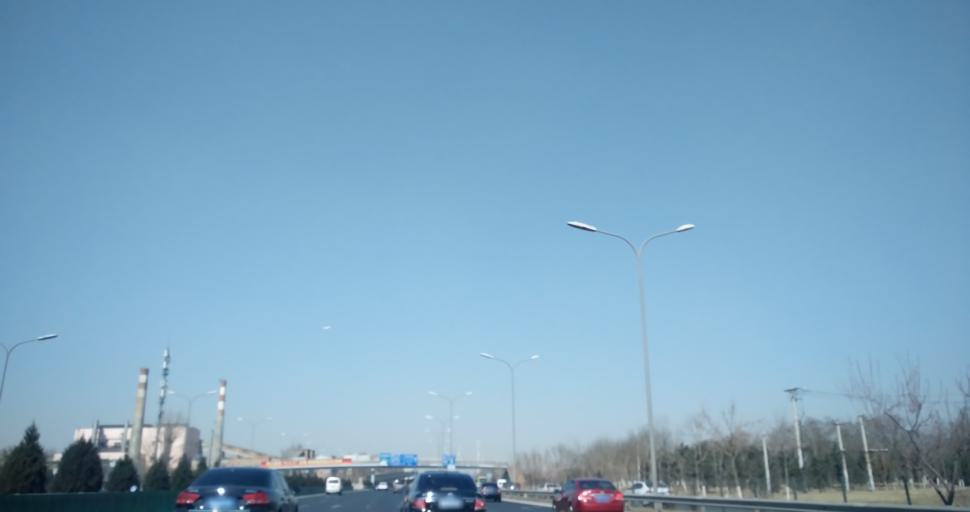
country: CN
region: Beijing
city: Jiugong
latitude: 39.7920
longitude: 116.4240
